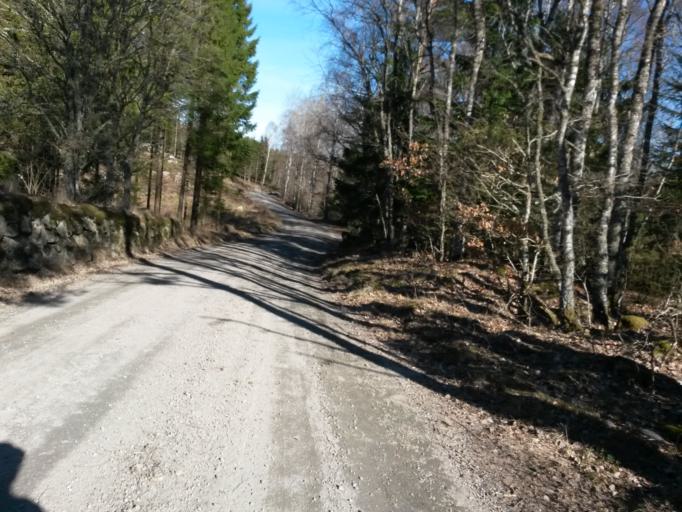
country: SE
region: Vaestra Goetaland
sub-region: Vargarda Kommun
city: Jonstorp
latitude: 57.9699
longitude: 12.7359
